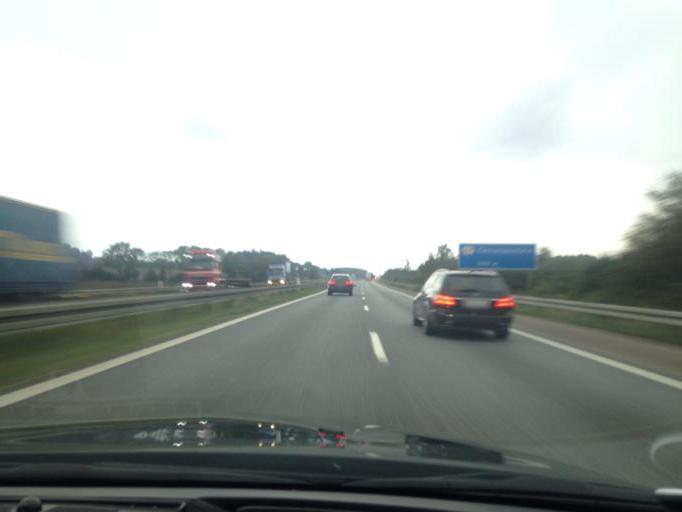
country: DK
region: South Denmark
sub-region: Kolding Kommune
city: Christiansfeld
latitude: 55.3500
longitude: 9.4456
